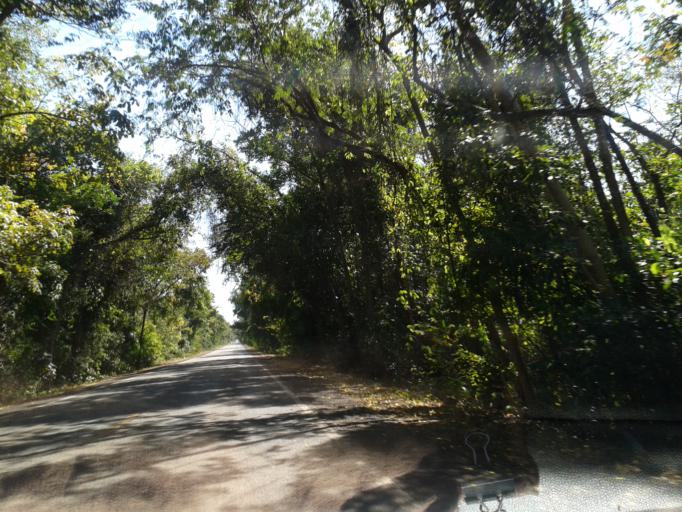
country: BR
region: Goias
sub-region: Crixas
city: Crixas
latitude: -14.0232
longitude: -50.3270
